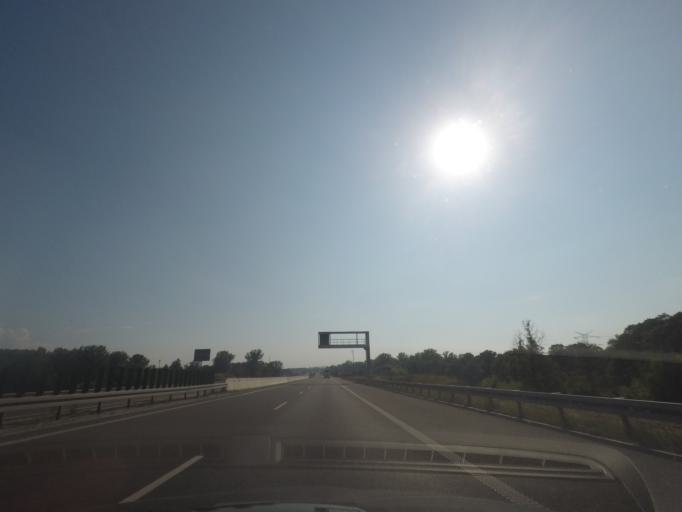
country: PL
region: Silesian Voivodeship
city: Gorzyczki
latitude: 49.9366
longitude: 18.4074
